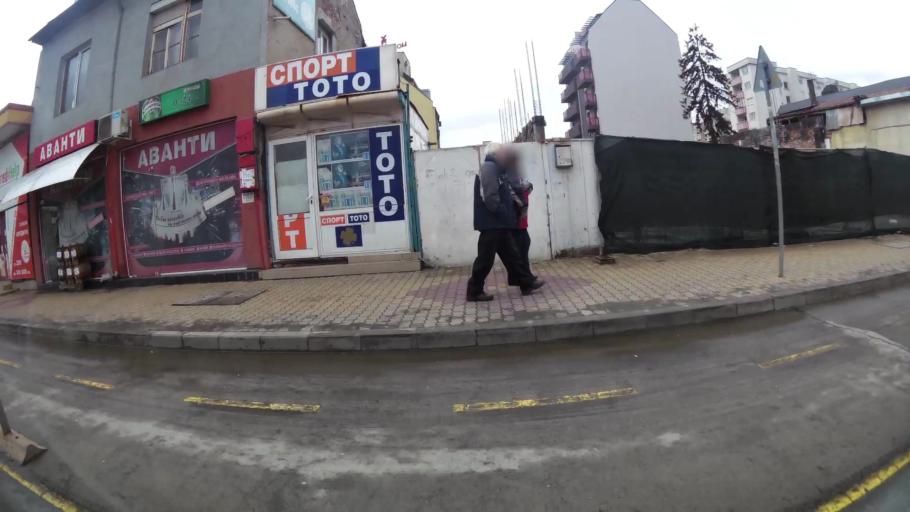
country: BG
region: Sofia-Capital
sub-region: Stolichna Obshtina
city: Sofia
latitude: 42.7282
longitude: 23.3006
